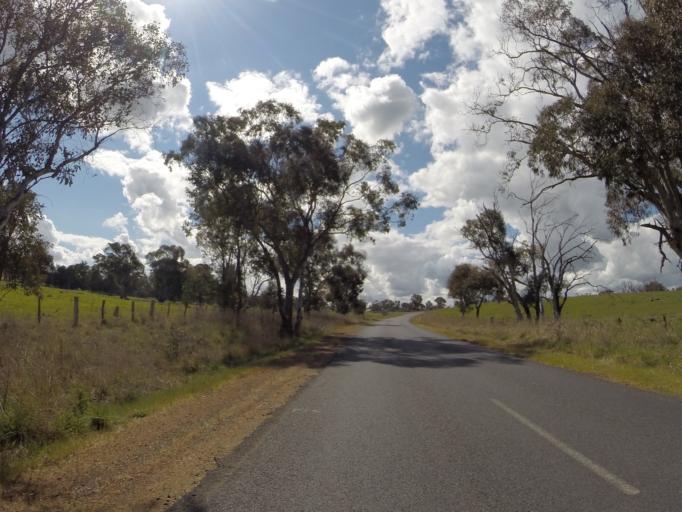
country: AU
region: New South Wales
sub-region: Yass Valley
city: Yass
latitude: -34.9418
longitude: 148.8724
